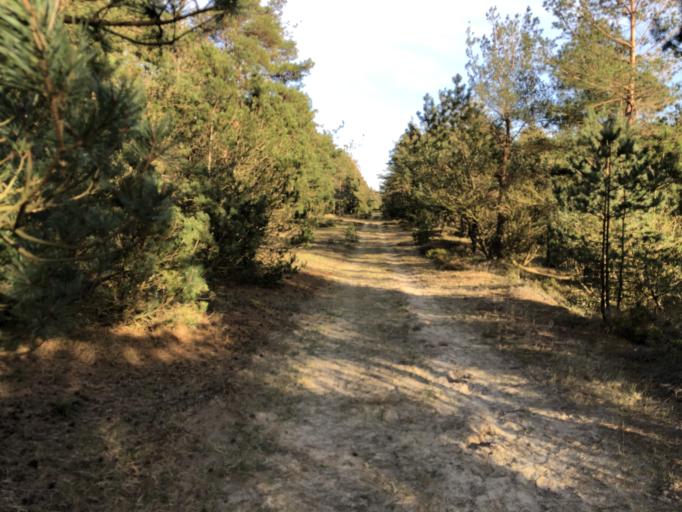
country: DK
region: Central Jutland
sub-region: Holstebro Kommune
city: Ulfborg
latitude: 56.2481
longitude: 8.4371
